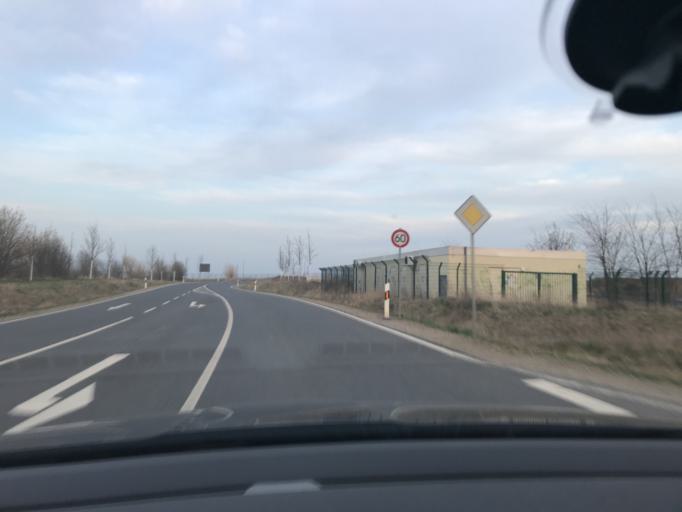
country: DE
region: Brandenburg
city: Schonefeld
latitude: 52.3630
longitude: 13.4738
